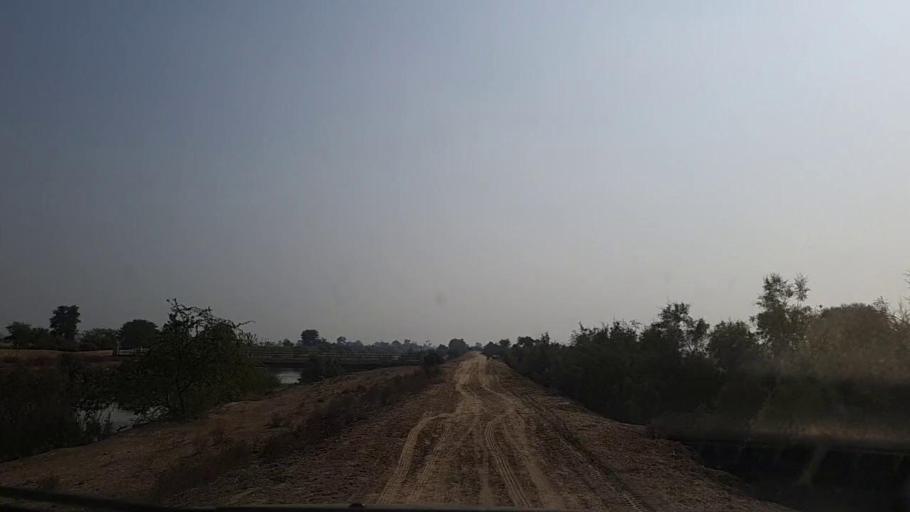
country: PK
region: Sindh
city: Sanghar
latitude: 26.0369
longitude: 68.9978
